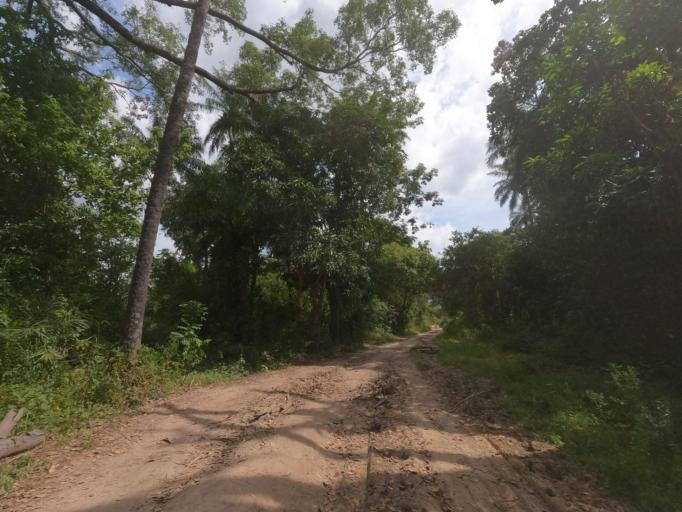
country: GW
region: Oio
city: Bissora
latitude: 12.4443
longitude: -15.5510
